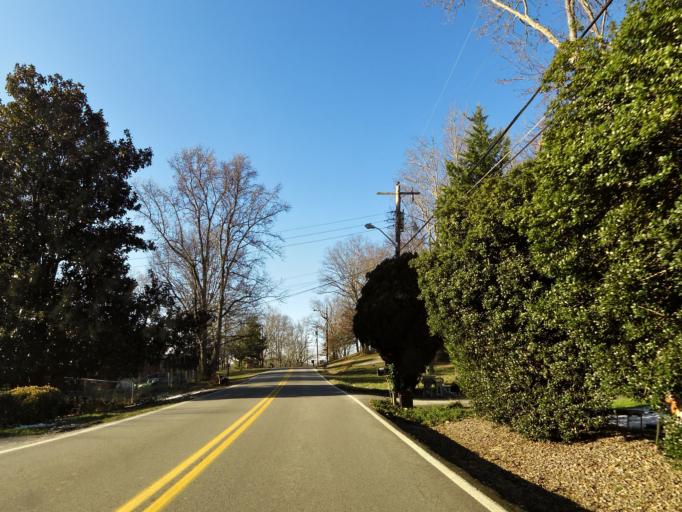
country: US
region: Tennessee
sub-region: Knox County
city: Farragut
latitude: 35.9489
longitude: -84.0492
